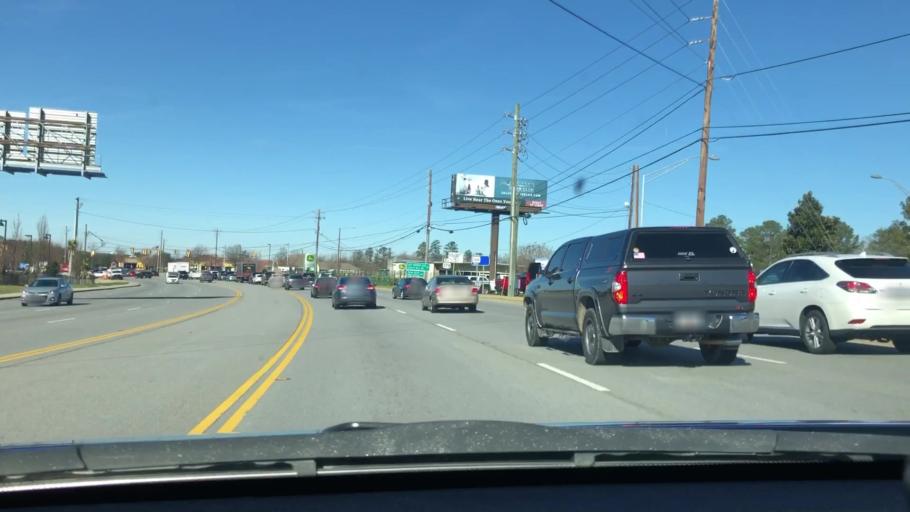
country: US
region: South Carolina
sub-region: Lexington County
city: Oak Grove
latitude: 34.0128
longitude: -81.1508
